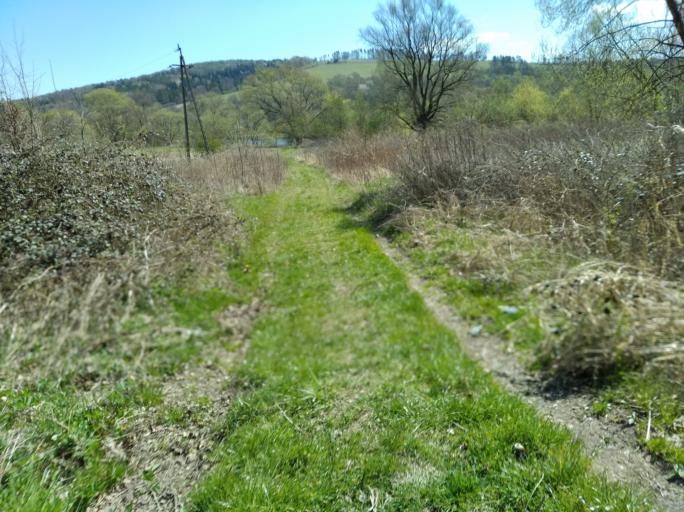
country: PL
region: Subcarpathian Voivodeship
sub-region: Powiat brzozowski
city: Dydnia
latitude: 49.7132
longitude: 22.2044
